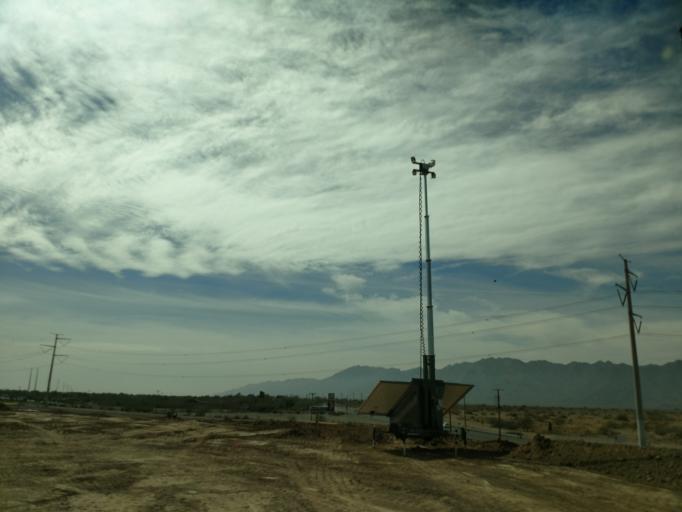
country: US
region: Arizona
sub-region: Maricopa County
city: Laveen
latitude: 33.3266
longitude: -112.1685
